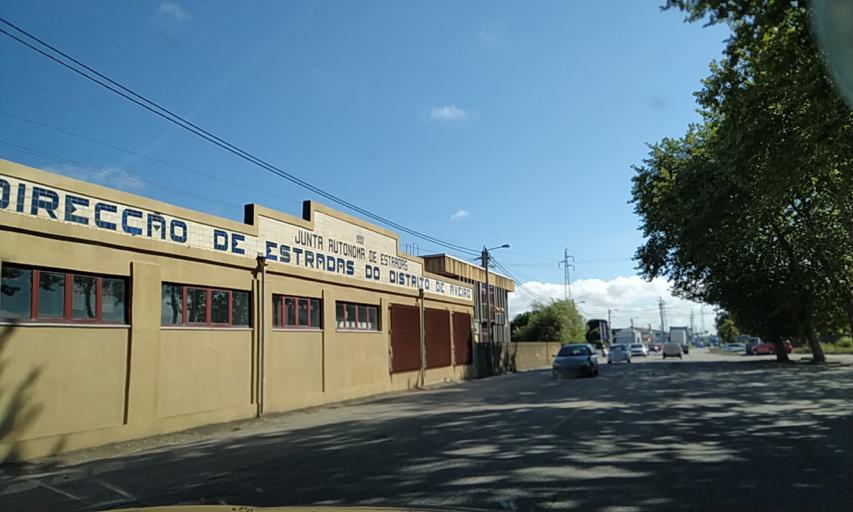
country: PT
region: Aveiro
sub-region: Aveiro
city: Aveiro
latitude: 40.6605
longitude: -8.6139
